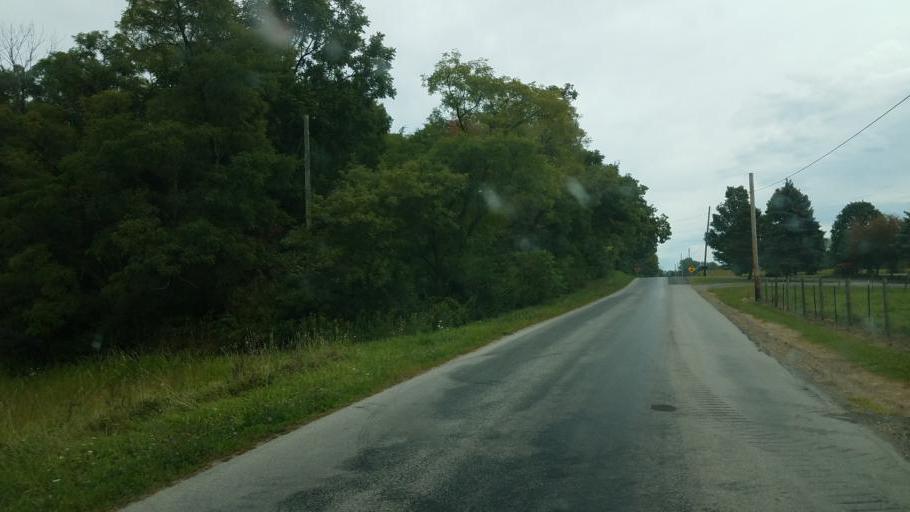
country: US
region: Ohio
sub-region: Knox County
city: Centerburg
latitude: 40.3201
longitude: -82.6959
